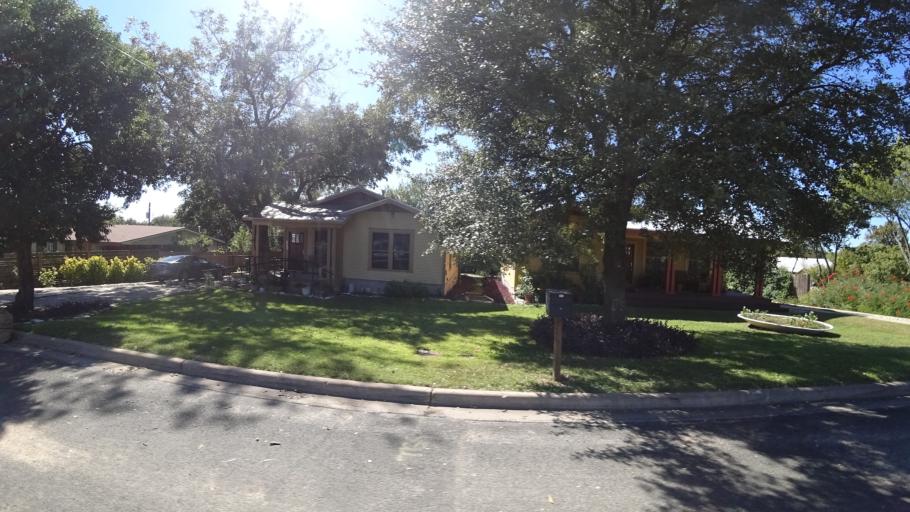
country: US
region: Texas
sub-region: Travis County
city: Austin
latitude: 30.2860
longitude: -97.6994
